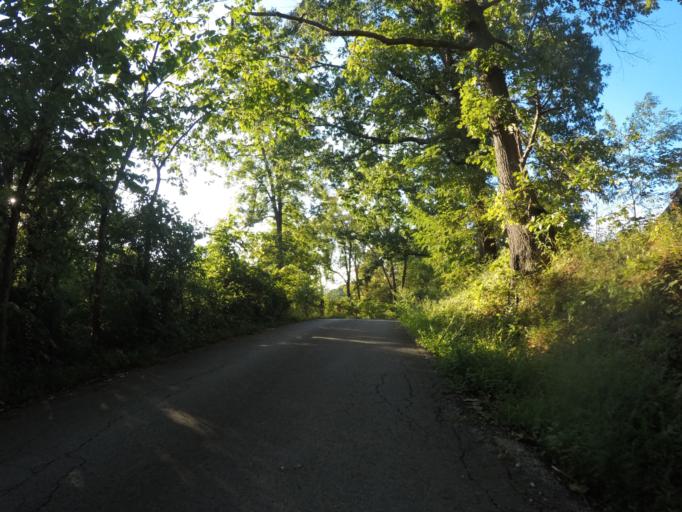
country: US
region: Ohio
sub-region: Lawrence County
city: Coal Grove
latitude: 38.5838
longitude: -82.5490
